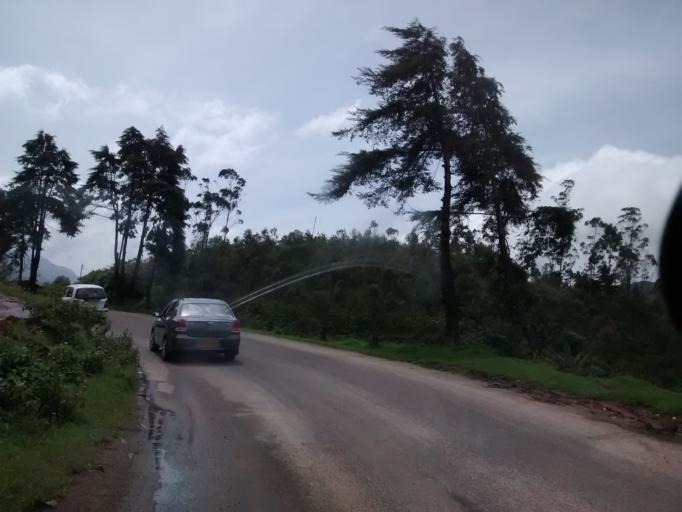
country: IN
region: Kerala
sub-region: Idukki
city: Munnar
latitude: 10.0883
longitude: 77.0830
